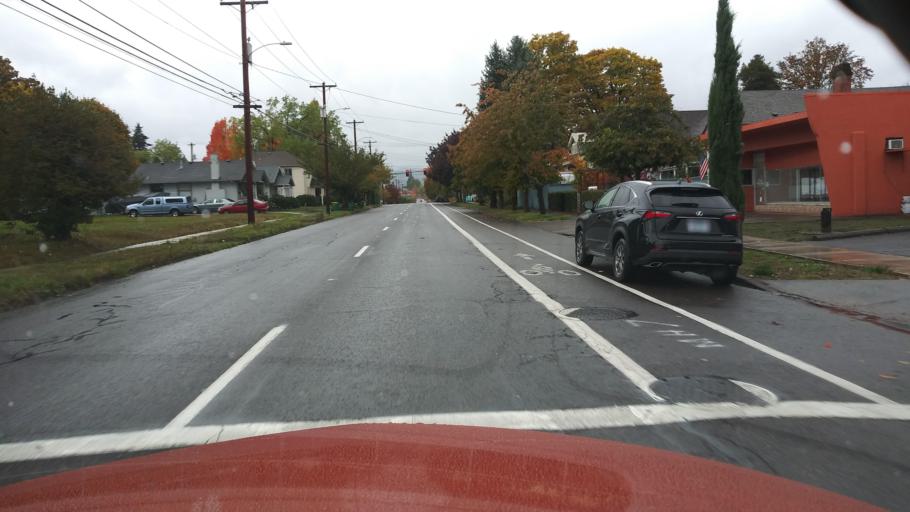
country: US
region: Oregon
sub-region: Washington County
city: Forest Grove
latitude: 45.5196
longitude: -123.1012
